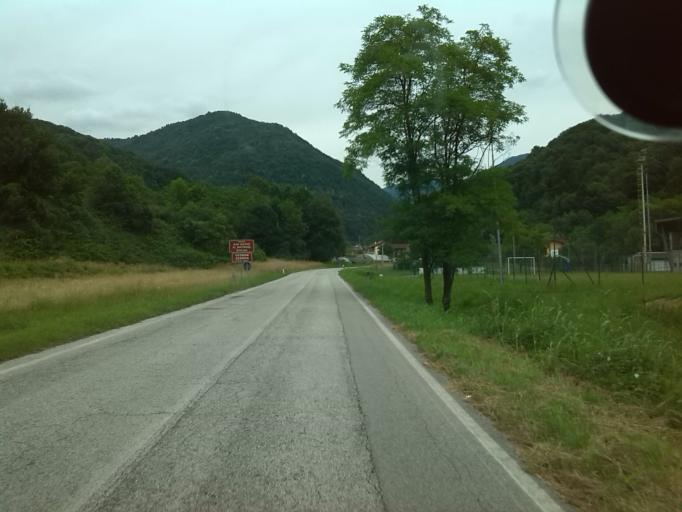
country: IT
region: Friuli Venezia Giulia
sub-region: Provincia di Udine
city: Savogna
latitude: 46.1549
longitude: 13.5258
